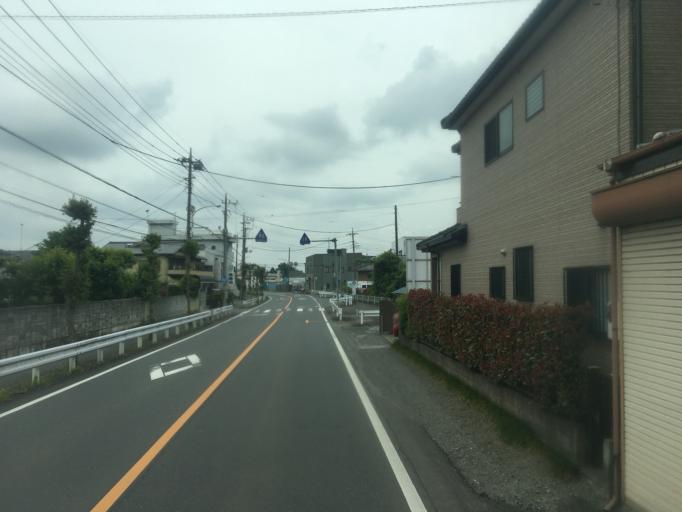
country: JP
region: Saitama
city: Kawagoe
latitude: 35.9722
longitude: 139.4623
